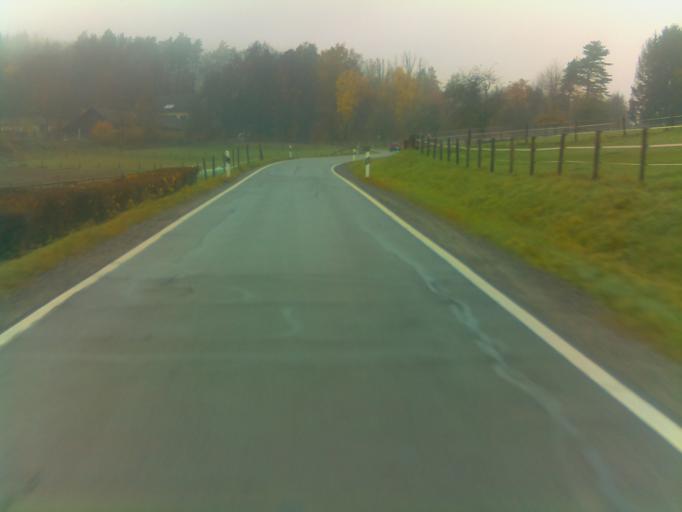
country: DE
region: Hesse
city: Neckarsteinach
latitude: 49.4211
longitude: 8.8553
